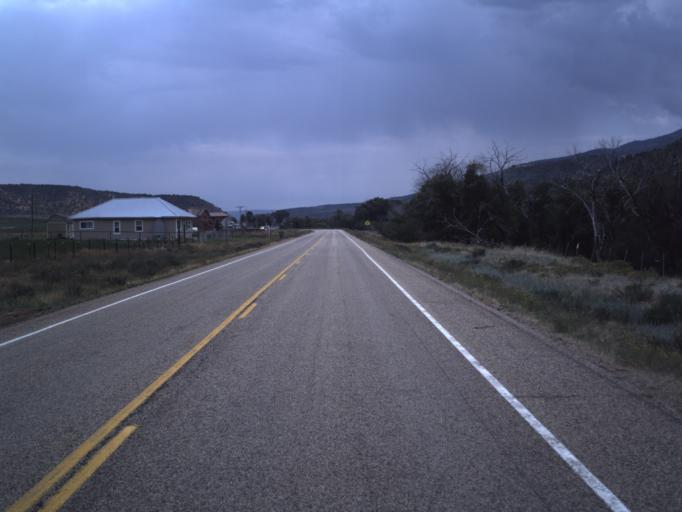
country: US
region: Utah
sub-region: Duchesne County
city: Duchesne
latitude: 40.4378
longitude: -110.8114
